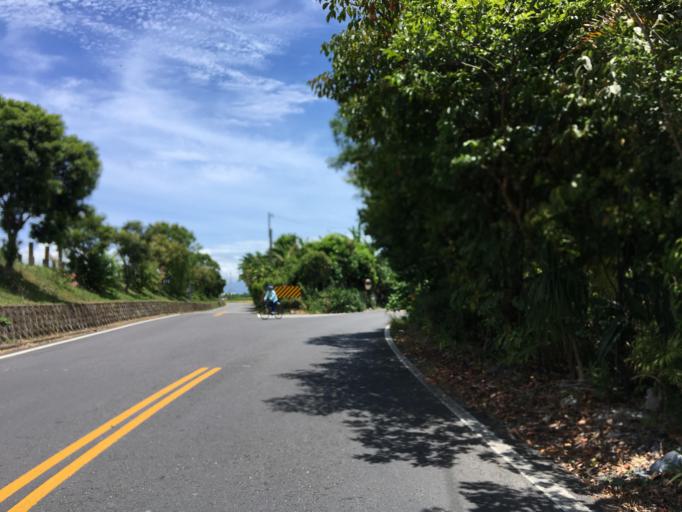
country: TW
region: Taiwan
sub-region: Yilan
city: Yilan
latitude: 24.6528
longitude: 121.7272
